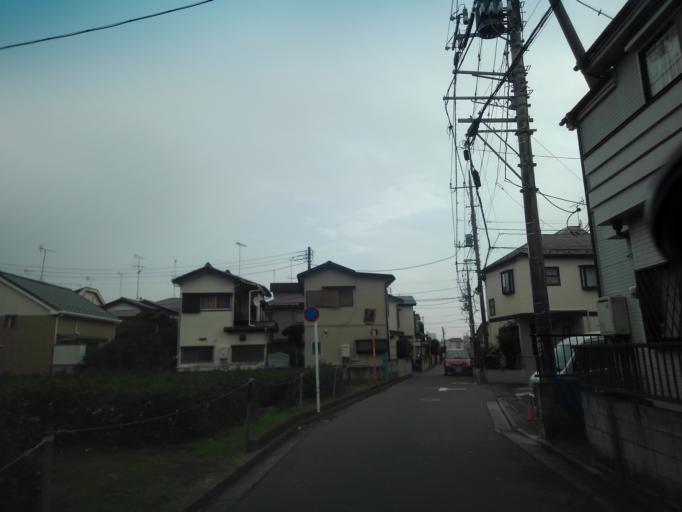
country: JP
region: Saitama
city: Tokorozawa
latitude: 35.7957
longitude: 139.4499
